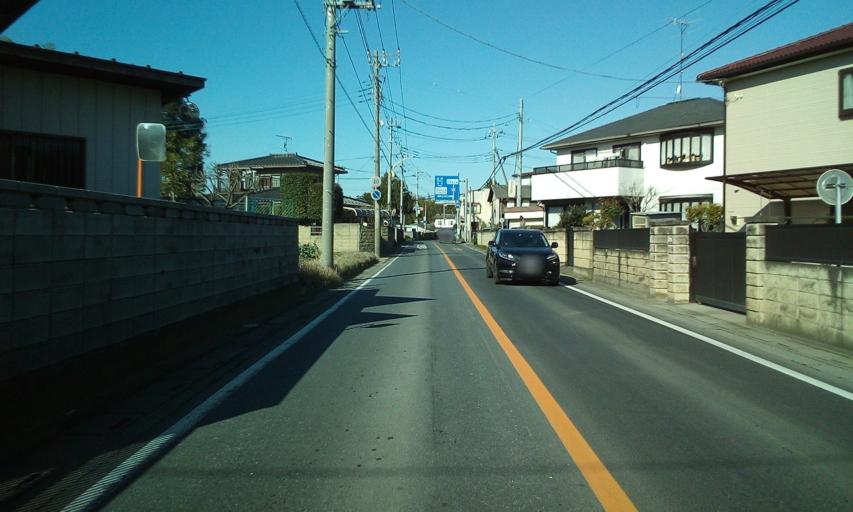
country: JP
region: Chiba
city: Noda
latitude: 35.9529
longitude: 139.8332
